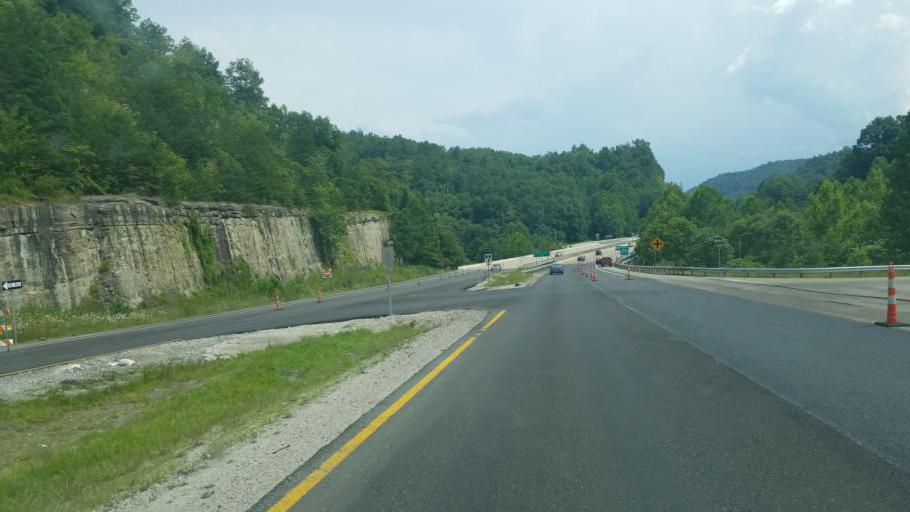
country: US
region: West Virginia
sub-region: Kanawha County
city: Alum Creek
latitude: 38.2246
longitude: -81.8360
